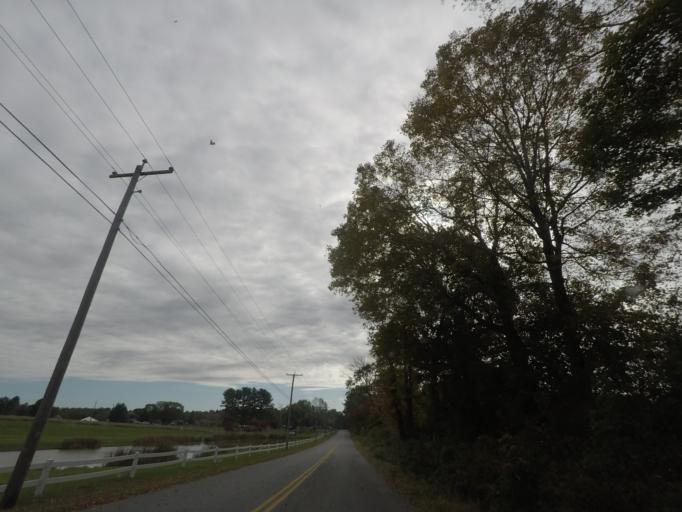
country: US
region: Connecticut
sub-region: Windham County
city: Thompson
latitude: 41.9512
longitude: -71.8449
